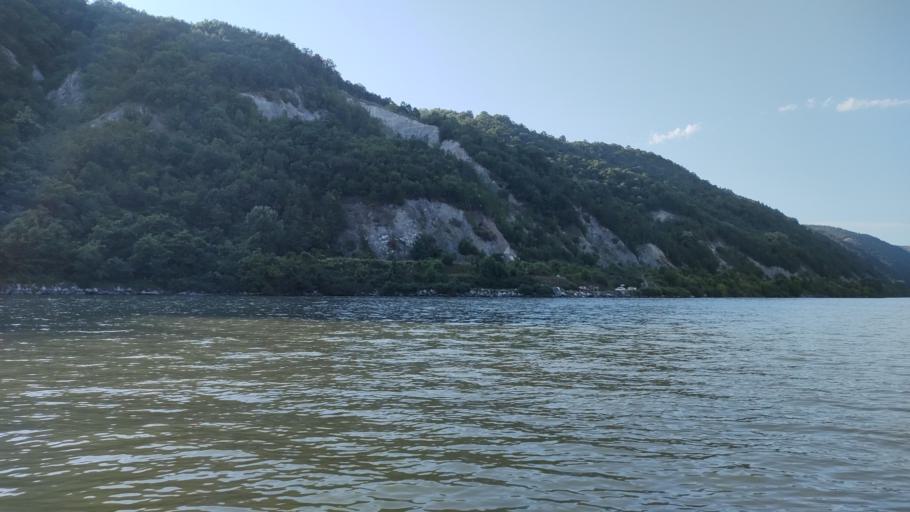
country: RO
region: Mehedinti
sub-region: Comuna Svinita
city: Svinita
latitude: 44.4870
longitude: 22.1831
